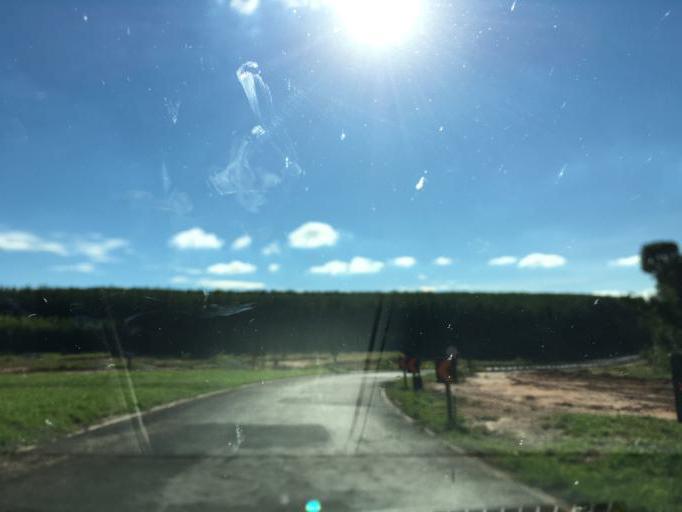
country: BR
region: Sao Paulo
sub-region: Duartina
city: Duartina
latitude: -22.5110
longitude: -49.3021
